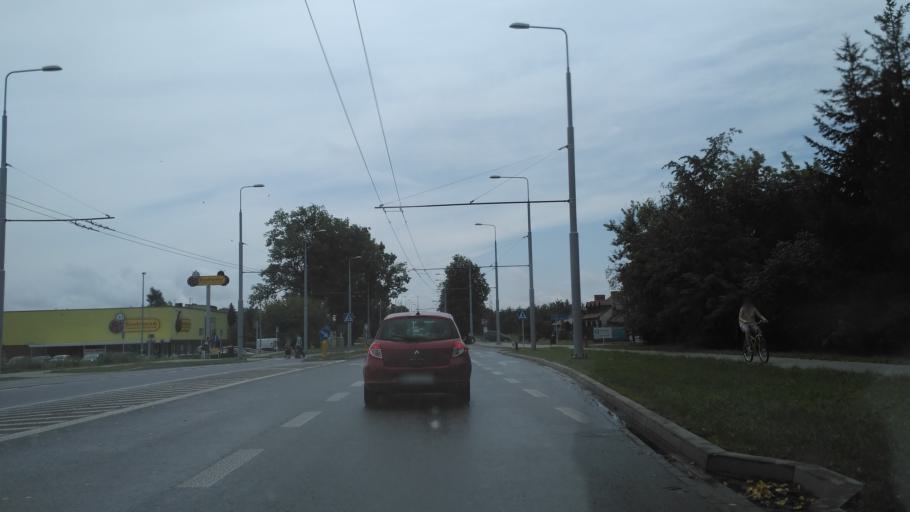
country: PL
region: Lublin Voivodeship
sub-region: Powiat lubelski
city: Lublin
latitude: 51.2014
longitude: 22.5859
